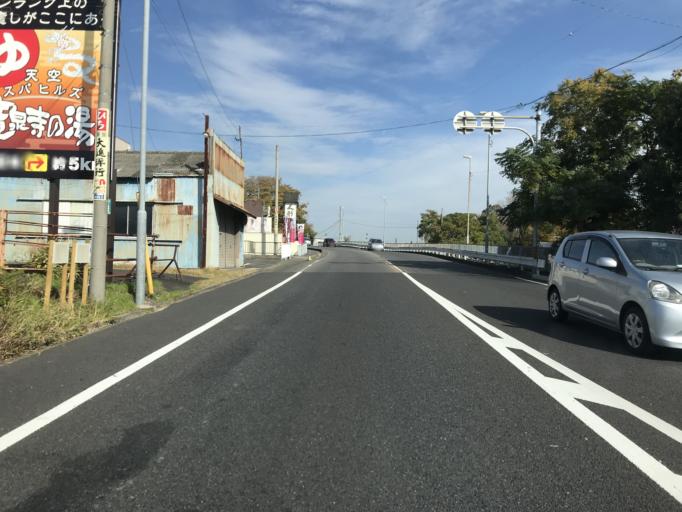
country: JP
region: Aichi
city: Nagoya-shi
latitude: 35.2133
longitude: 136.9332
